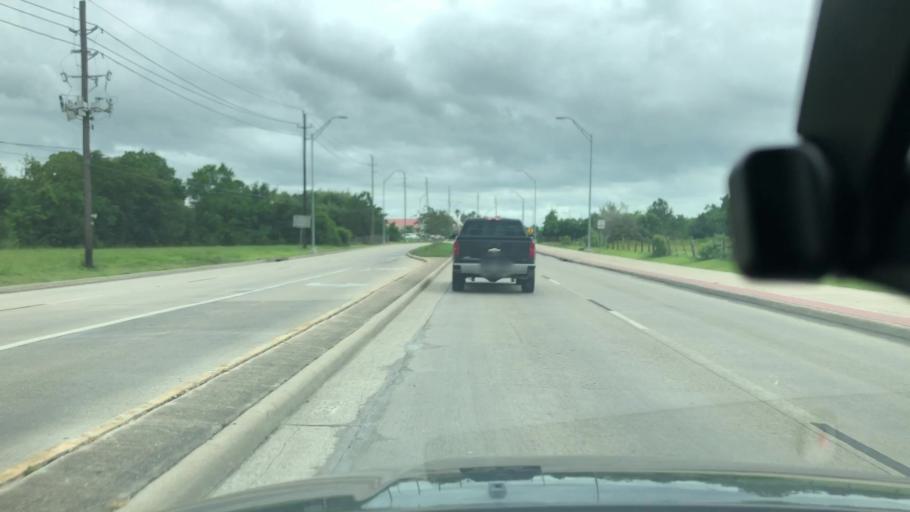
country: US
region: Texas
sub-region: Brazoria County
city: Brookside Village
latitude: 29.5809
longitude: -95.3517
